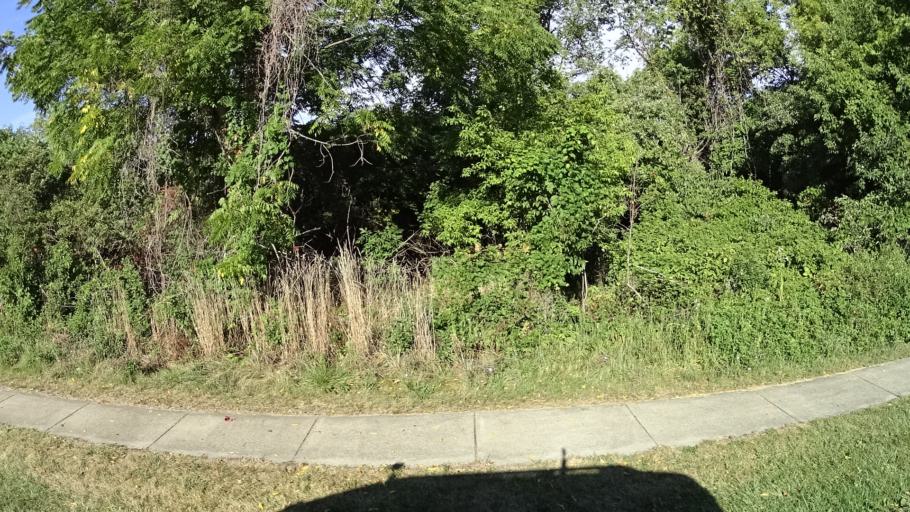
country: US
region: Ohio
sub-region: Erie County
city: Sandusky
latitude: 41.6092
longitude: -82.7080
